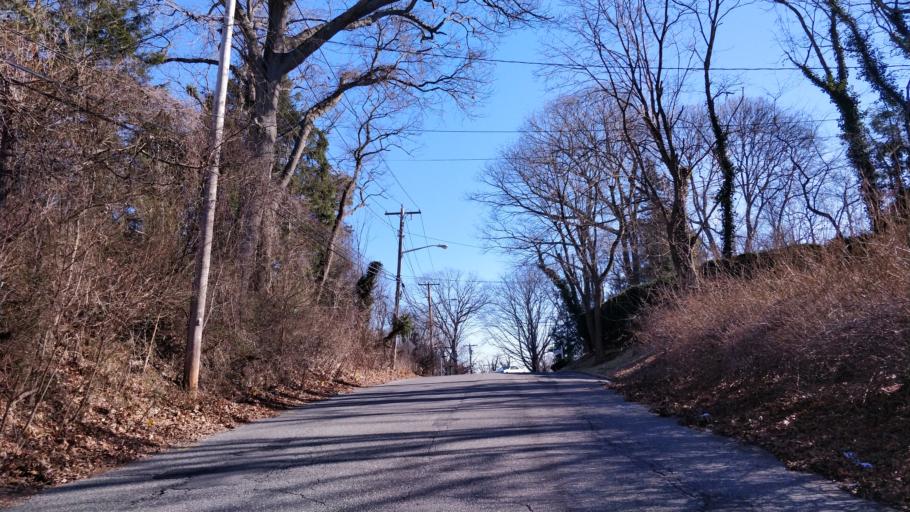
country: US
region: New York
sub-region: Suffolk County
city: East Setauket
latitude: 40.9401
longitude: -73.0960
